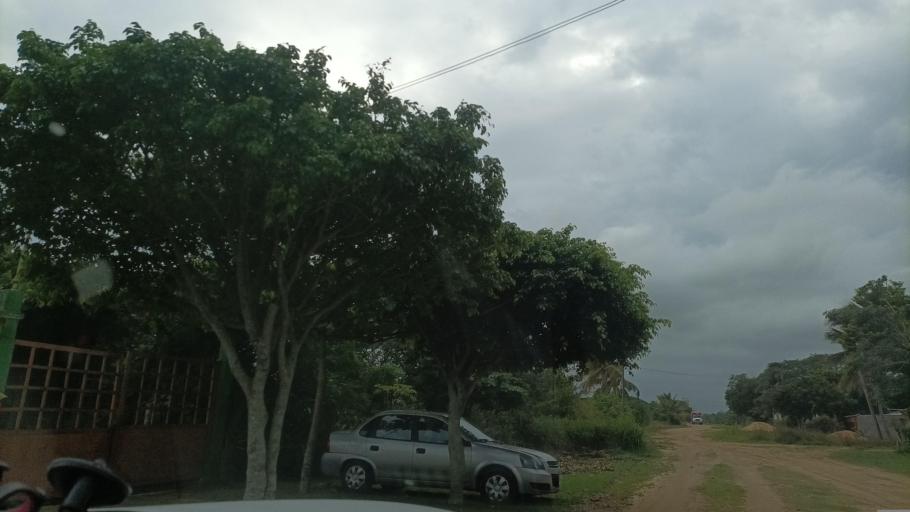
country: MX
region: Veracruz
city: Agua Dulce
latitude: 18.2070
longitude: -94.1435
